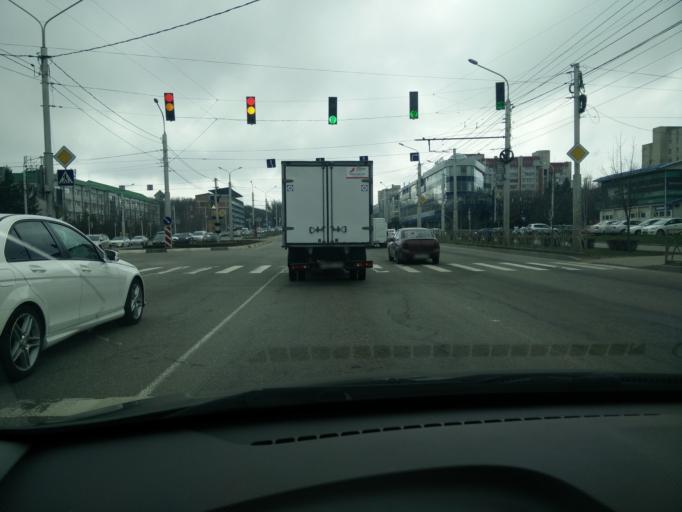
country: RU
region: Stavropol'skiy
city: Stavropol'
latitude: 45.0129
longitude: 41.9302
